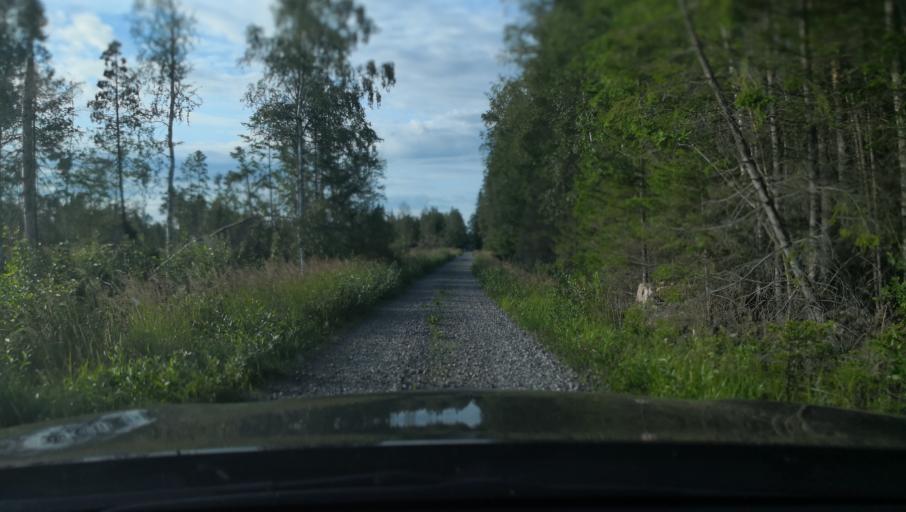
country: SE
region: Uppsala
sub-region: Osthammars Kommun
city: Osterbybruk
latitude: 60.0347
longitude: 17.9194
